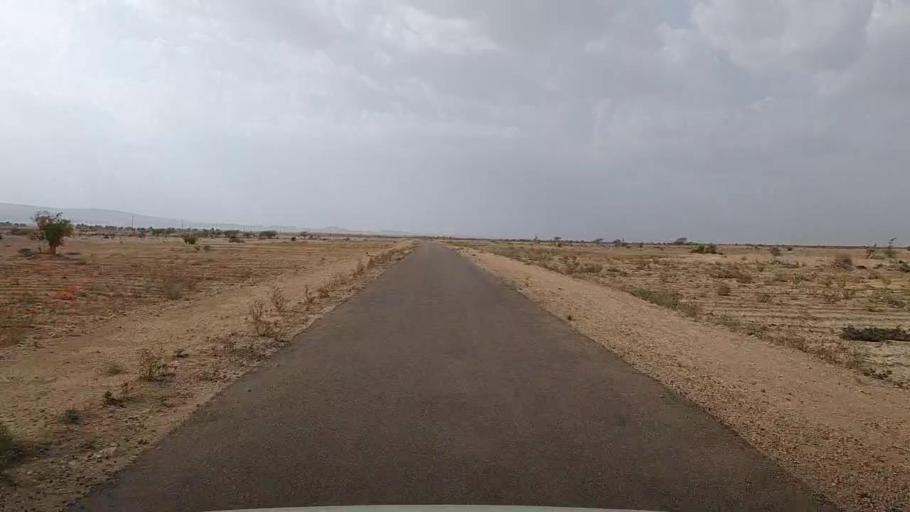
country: PK
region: Sindh
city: Jamshoro
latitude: 25.4406
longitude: 67.6834
